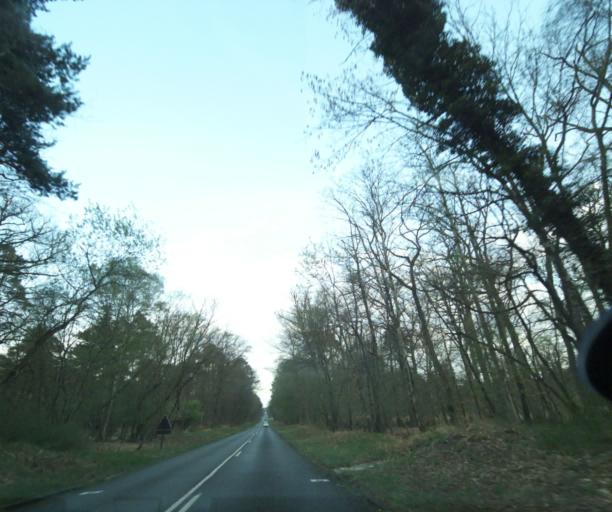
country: FR
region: Ile-de-France
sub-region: Departement de Seine-et-Marne
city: Avon
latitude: 48.3879
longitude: 2.7152
